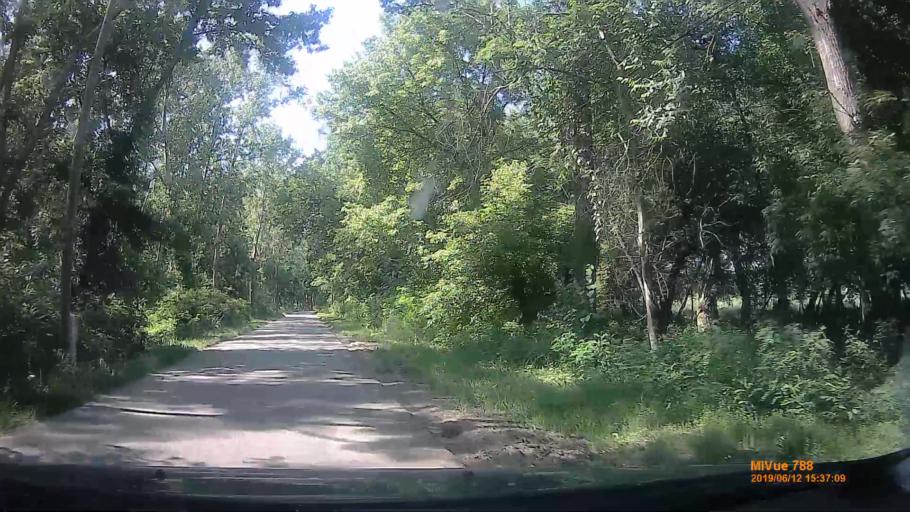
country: HU
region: Csongrad
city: Mako
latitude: 46.2041
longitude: 20.4652
